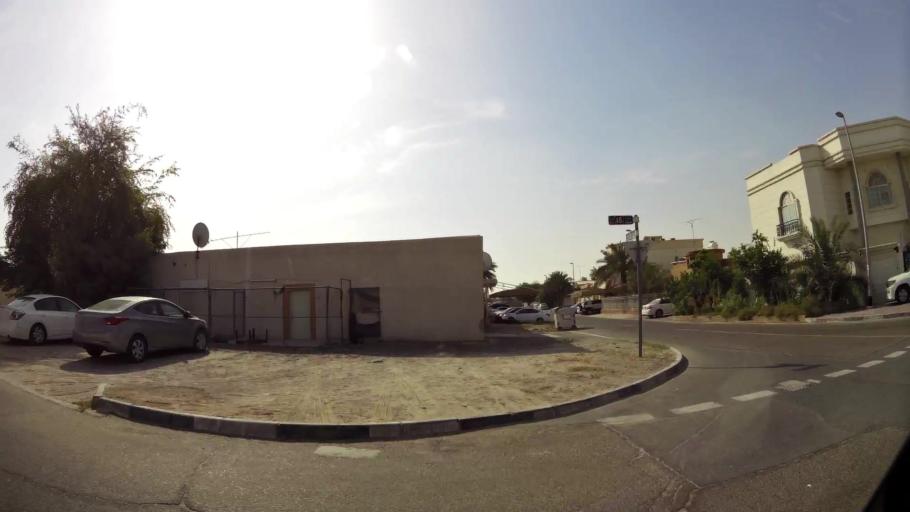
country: AE
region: Ash Shariqah
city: Sharjah
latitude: 25.2200
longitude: 55.3925
